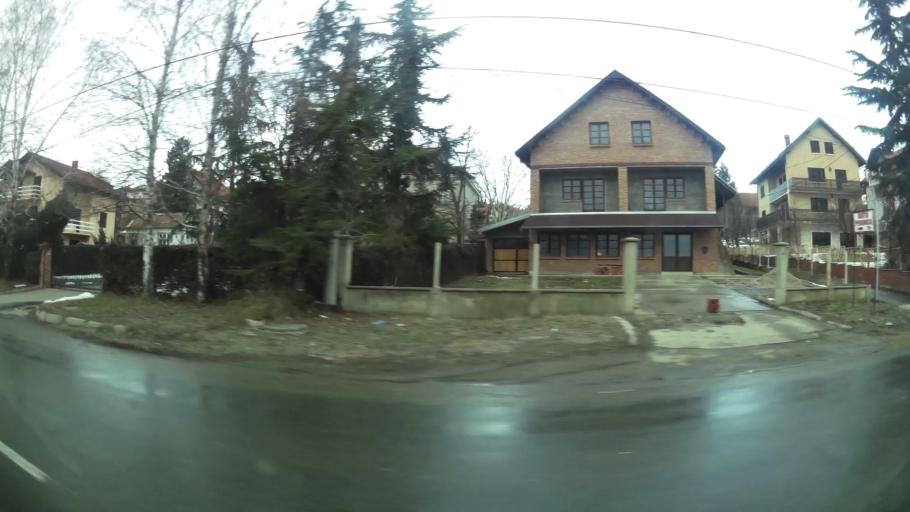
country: RS
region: Central Serbia
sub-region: Belgrade
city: Vozdovac
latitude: 44.7422
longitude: 20.4841
